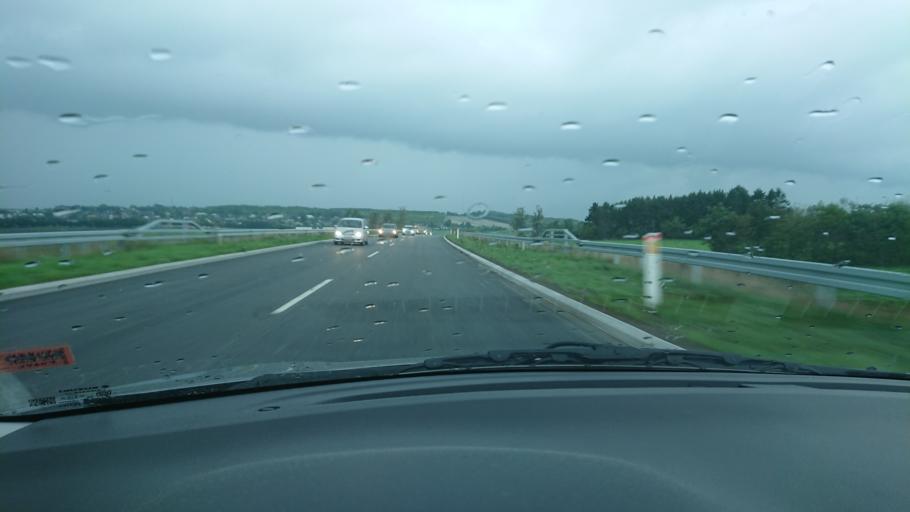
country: DK
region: North Denmark
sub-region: Alborg Kommune
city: Gistrup
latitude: 57.0001
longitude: 9.9431
